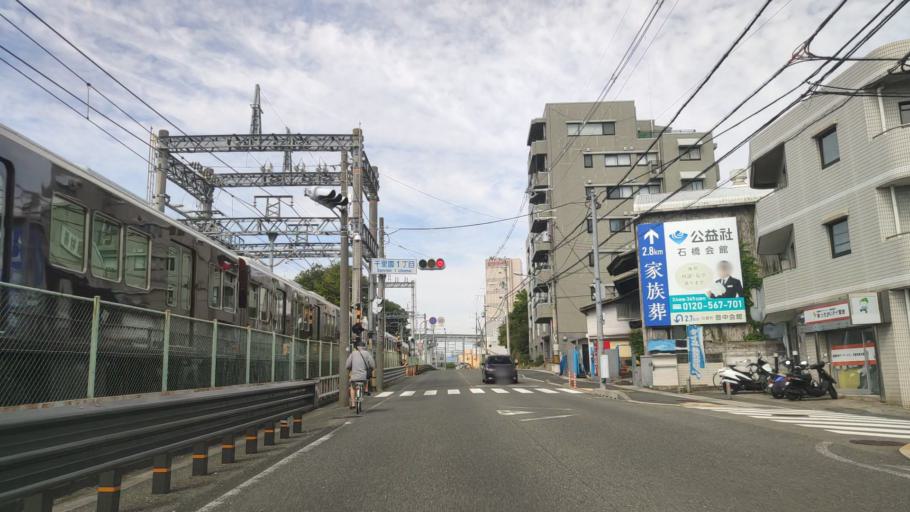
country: JP
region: Osaka
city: Toyonaka
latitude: 34.7910
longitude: 135.4532
